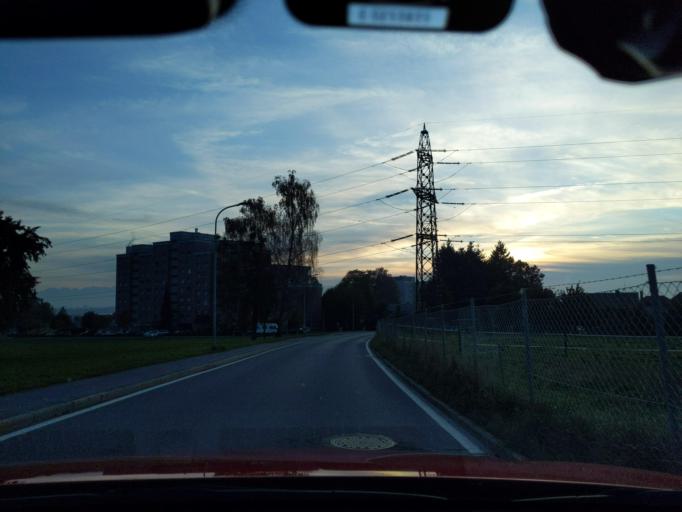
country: AT
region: Vorarlberg
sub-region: Politischer Bezirk Bregenz
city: Lochau
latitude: 47.5345
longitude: 9.7554
